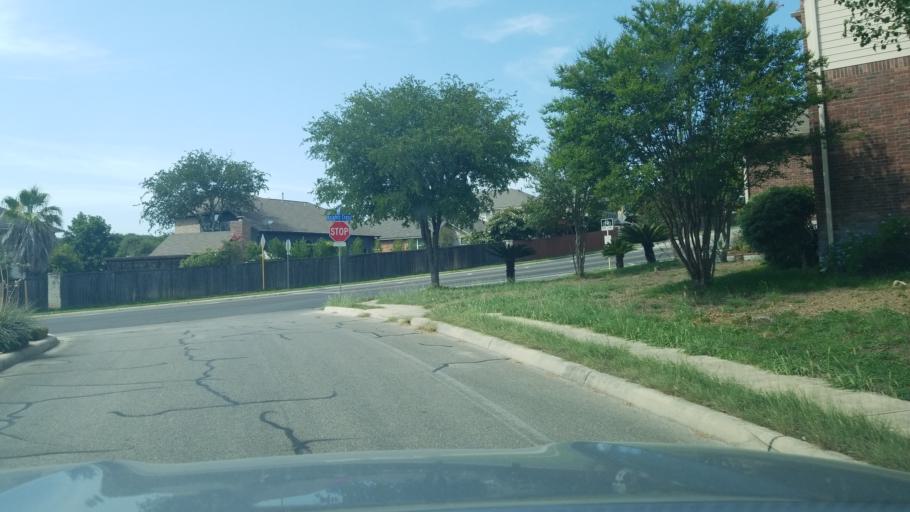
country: US
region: Texas
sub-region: Bexar County
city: Hollywood Park
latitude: 29.6323
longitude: -98.4892
